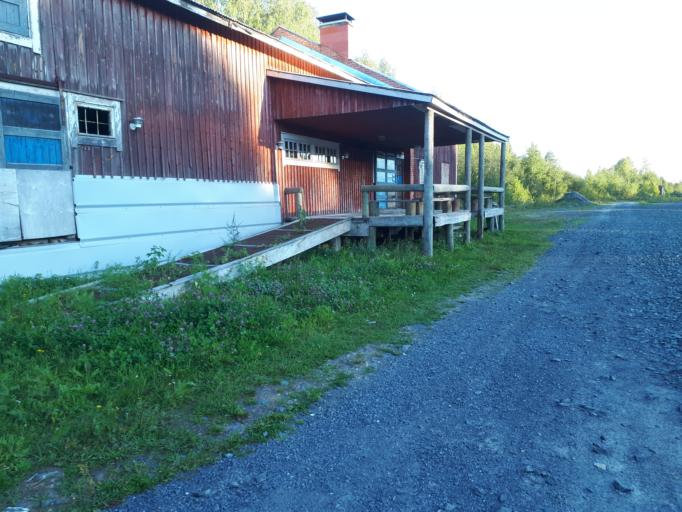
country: FI
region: Northern Ostrobothnia
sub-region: Oulunkaari
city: Ii
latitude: 65.3194
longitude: 25.4426
